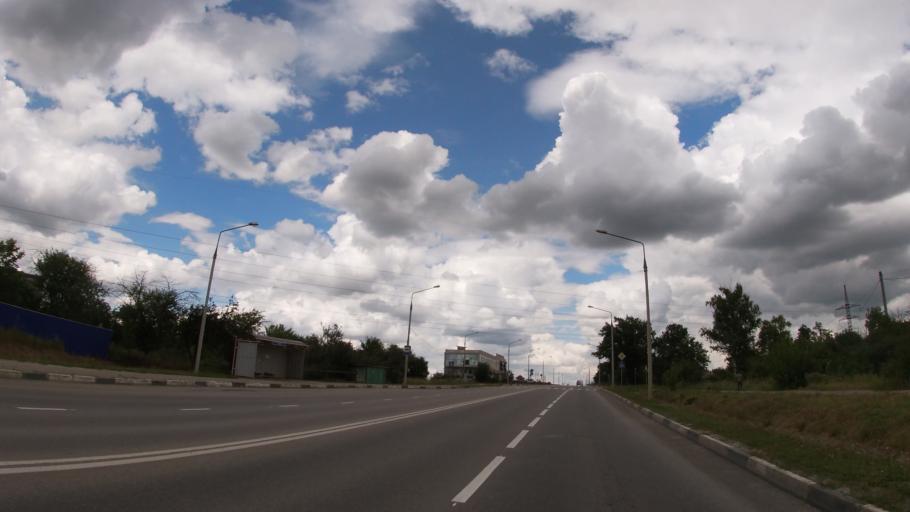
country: RU
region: Belgorod
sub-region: Belgorodskiy Rayon
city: Belgorod
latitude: 50.6251
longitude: 36.6116
